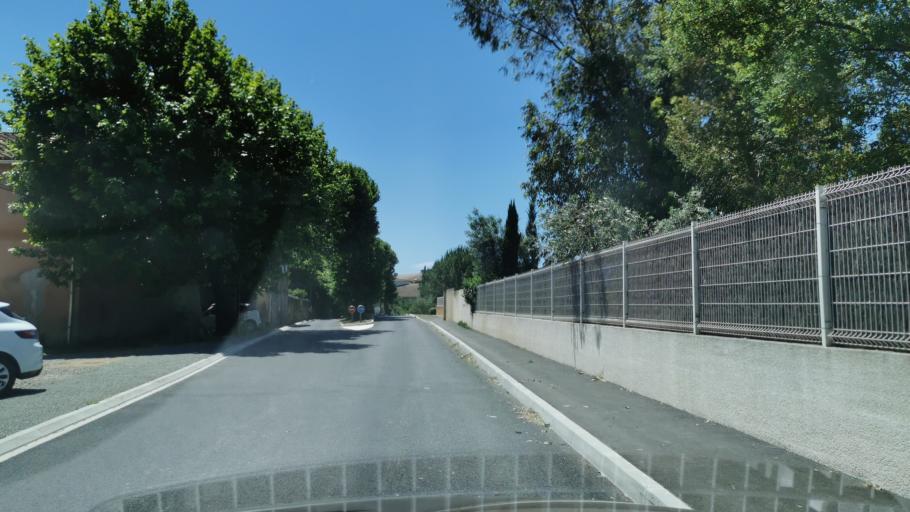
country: FR
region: Languedoc-Roussillon
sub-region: Departement de l'Aude
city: Saint-Marcel-sur-Aude
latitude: 43.2598
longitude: 2.9551
